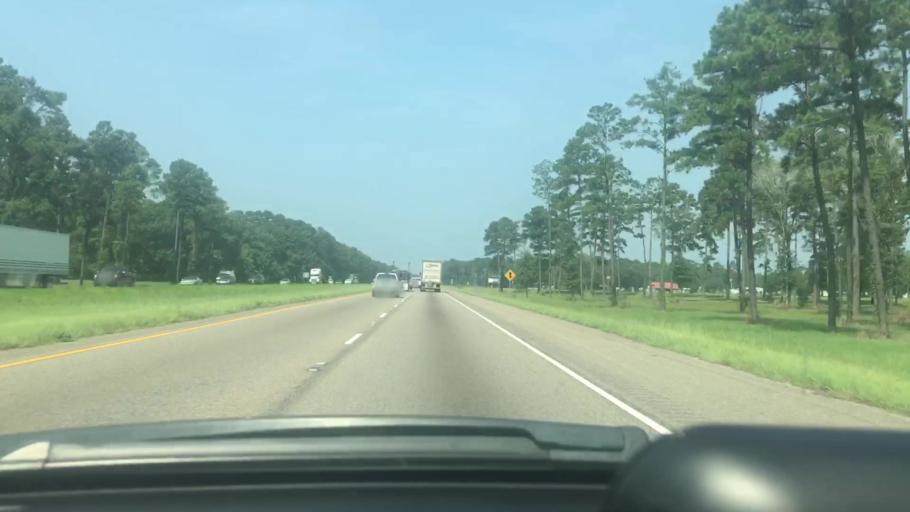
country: US
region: Louisiana
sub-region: Livingston Parish
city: Albany
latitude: 30.4748
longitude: -90.6433
